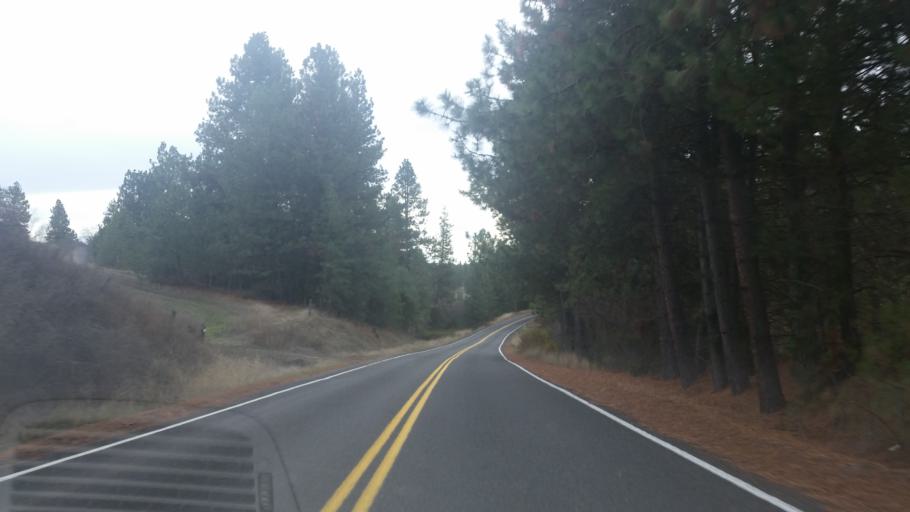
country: US
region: Washington
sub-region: Spokane County
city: Cheney
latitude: 47.2329
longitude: -117.4869
